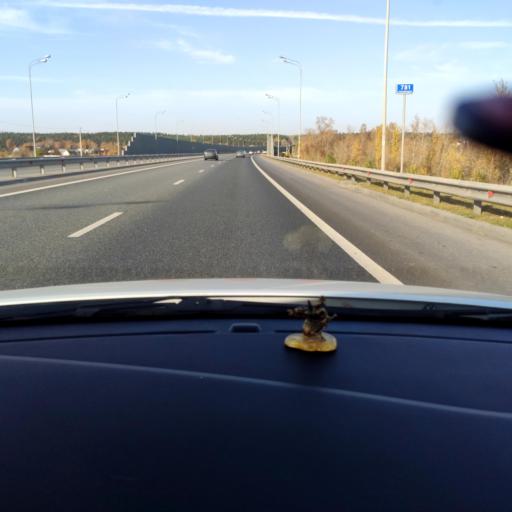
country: RU
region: Tatarstan
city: Osinovo
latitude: 55.8163
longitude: 48.8432
